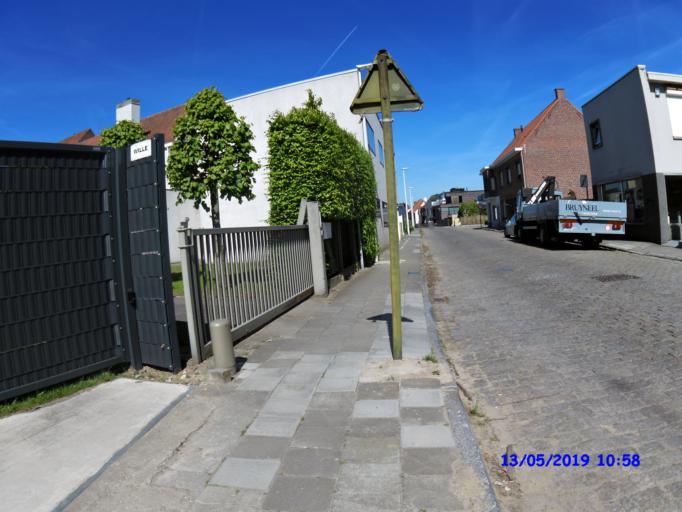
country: BE
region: Flanders
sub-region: Provincie West-Vlaanderen
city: Waregem
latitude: 50.8873
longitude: 3.4258
